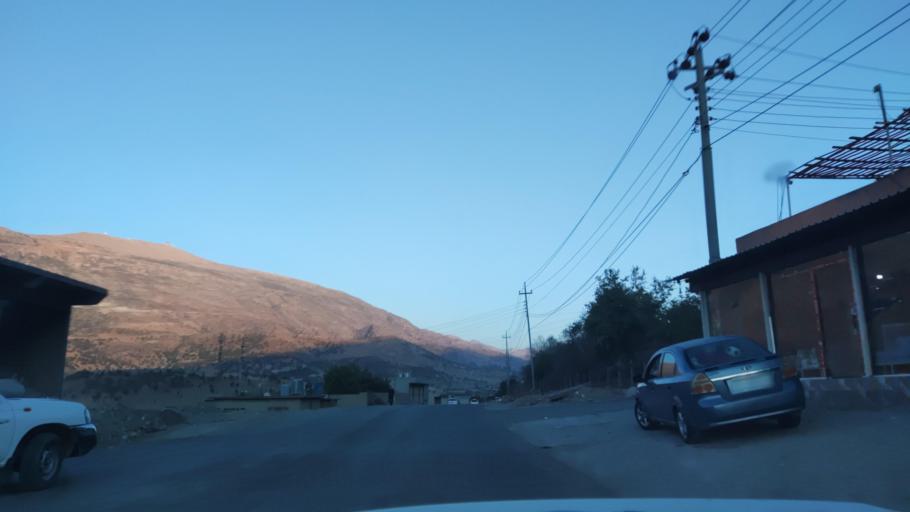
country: IQ
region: Arbil
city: Ruwandiz
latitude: 36.5900
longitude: 44.3899
